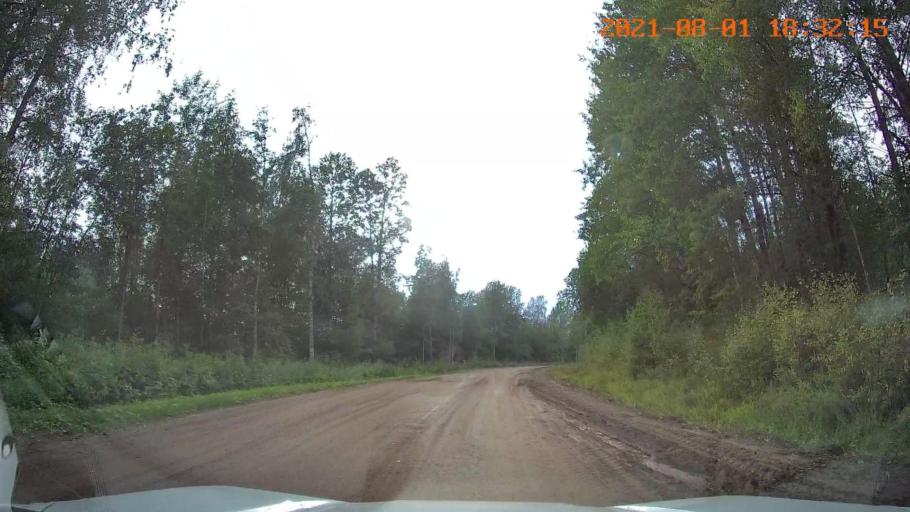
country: RU
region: Leningrad
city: Voznesen'ye
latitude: 60.8907
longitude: 35.3274
